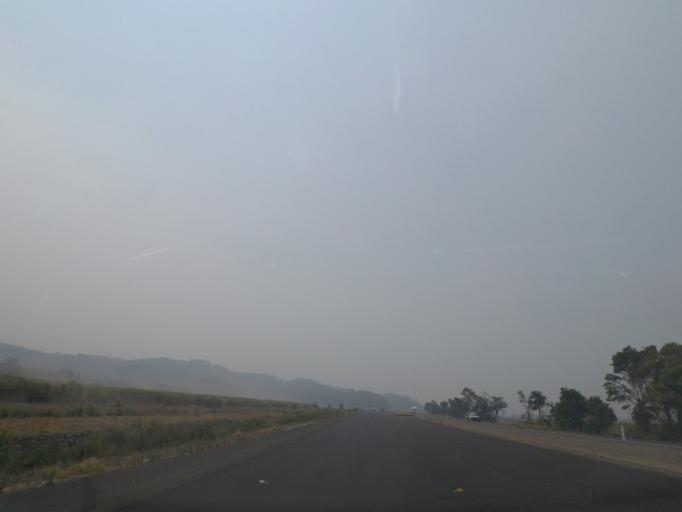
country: AU
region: New South Wales
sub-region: Ballina
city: Ballina
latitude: -28.8902
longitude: 153.4821
